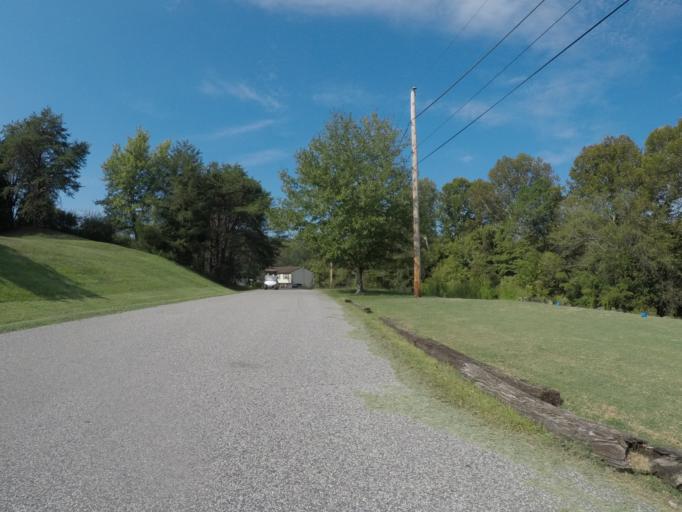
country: US
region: West Virginia
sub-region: Cabell County
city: Barboursville
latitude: 38.3636
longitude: -82.2764
